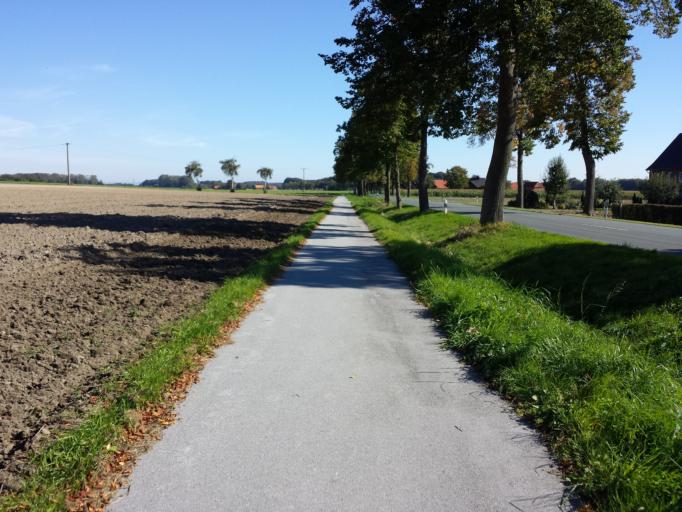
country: DE
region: North Rhine-Westphalia
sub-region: Regierungsbezirk Detmold
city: Langenberg
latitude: 51.7777
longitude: 8.3338
